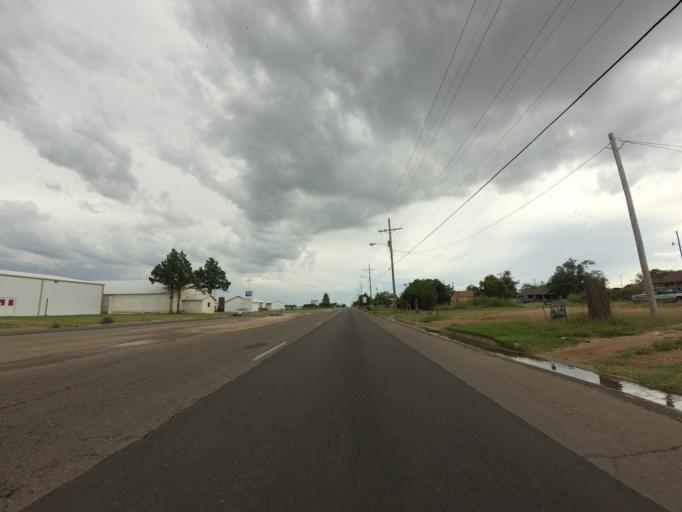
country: US
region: New Mexico
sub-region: Curry County
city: Clovis
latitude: 34.3810
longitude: -103.1966
